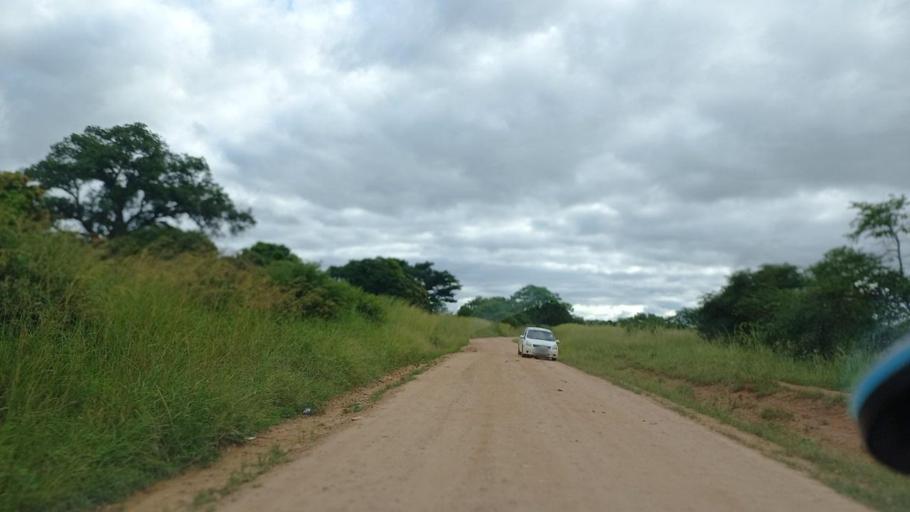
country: ZM
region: Lusaka
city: Chongwe
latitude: -15.4504
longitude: 28.8345
